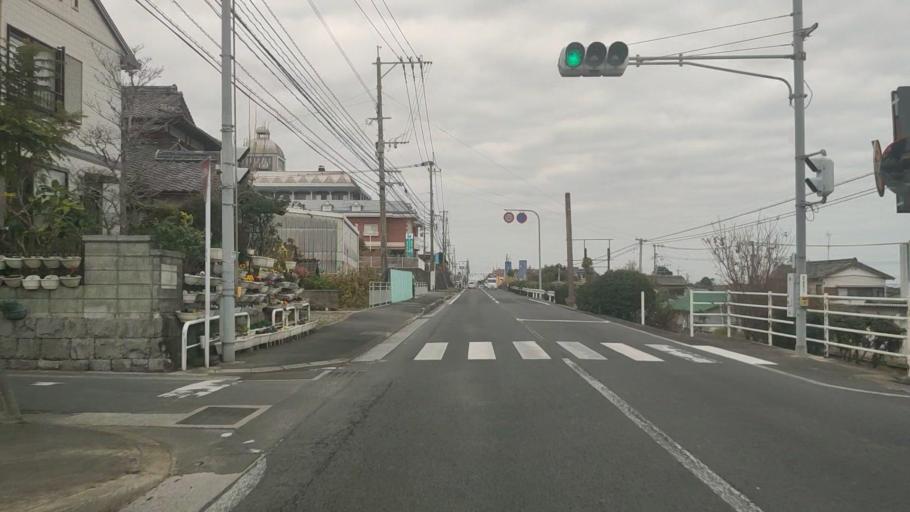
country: JP
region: Nagasaki
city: Shimabara
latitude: 32.8266
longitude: 130.3509
